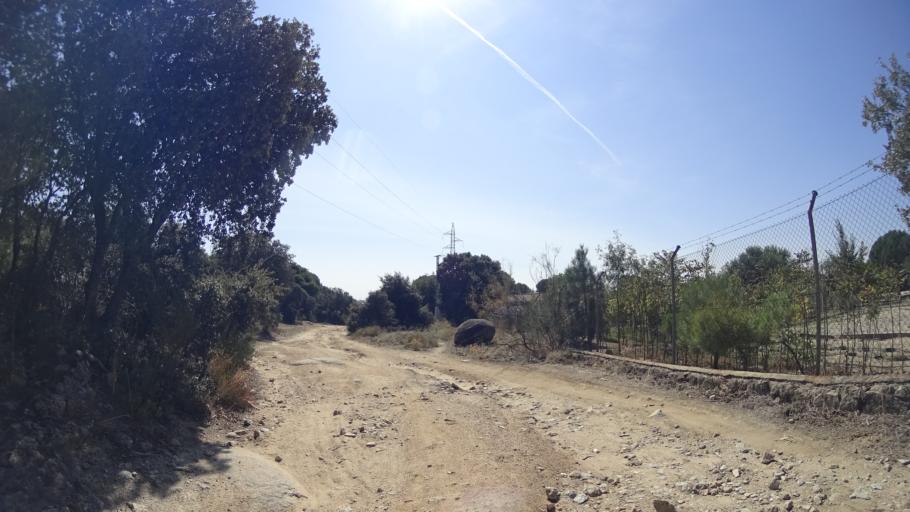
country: ES
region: Madrid
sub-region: Provincia de Madrid
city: Colmenarejo
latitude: 40.5732
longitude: -4.0259
